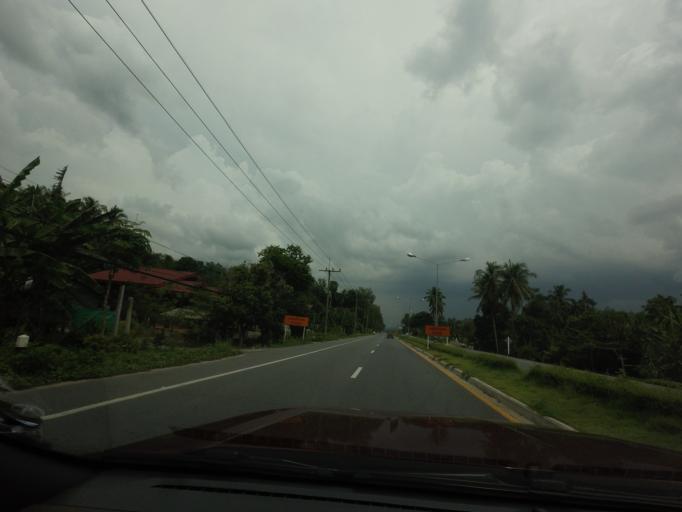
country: TH
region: Yala
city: Krong Pi Nang
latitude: 6.4598
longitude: 101.2735
